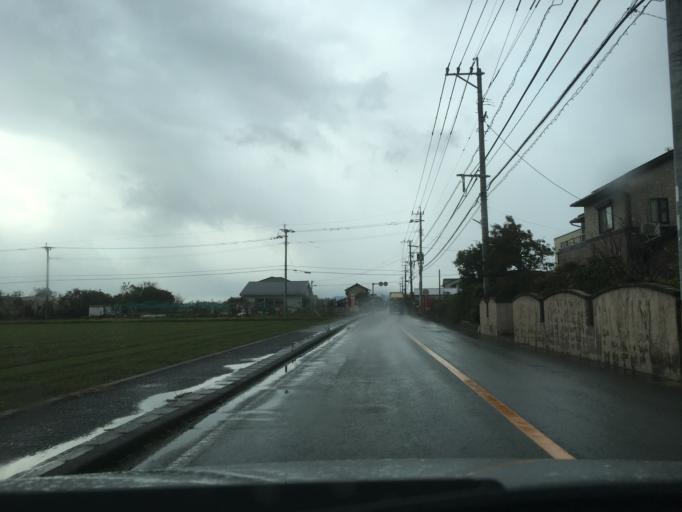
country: JP
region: Saga Prefecture
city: Tosu
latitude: 33.3778
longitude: 130.5678
